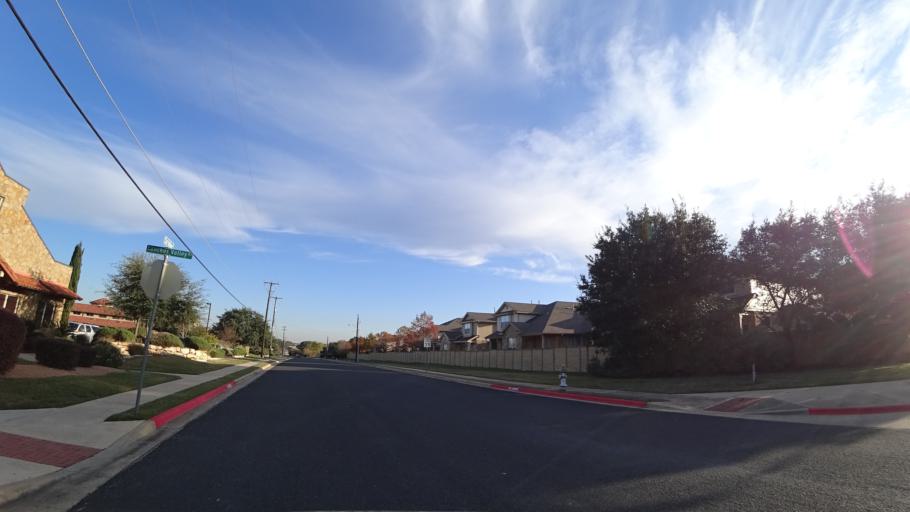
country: US
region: Texas
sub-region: Williamson County
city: Brushy Creek
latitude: 30.4971
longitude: -97.7270
